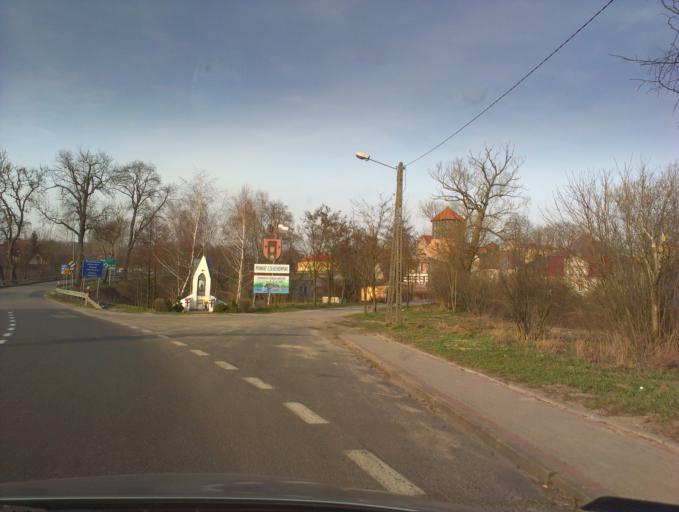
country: PL
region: Pomeranian Voivodeship
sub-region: Powiat czluchowski
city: Debrzno
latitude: 53.5337
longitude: 17.2312
